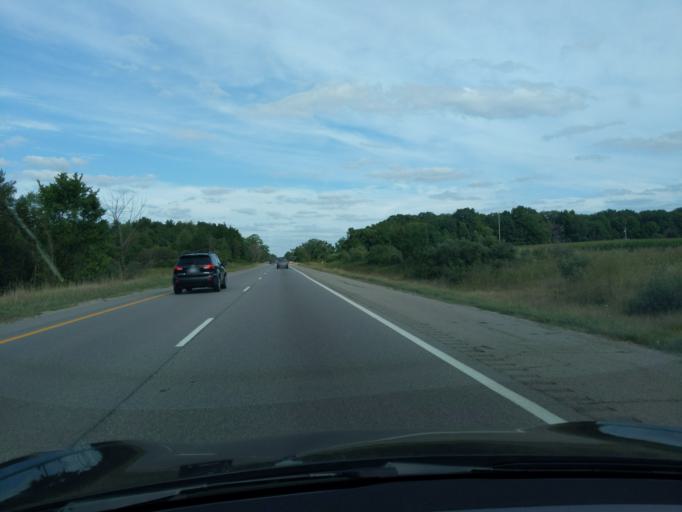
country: US
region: Michigan
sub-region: Ottawa County
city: Coopersville
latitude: 43.0699
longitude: -86.0218
